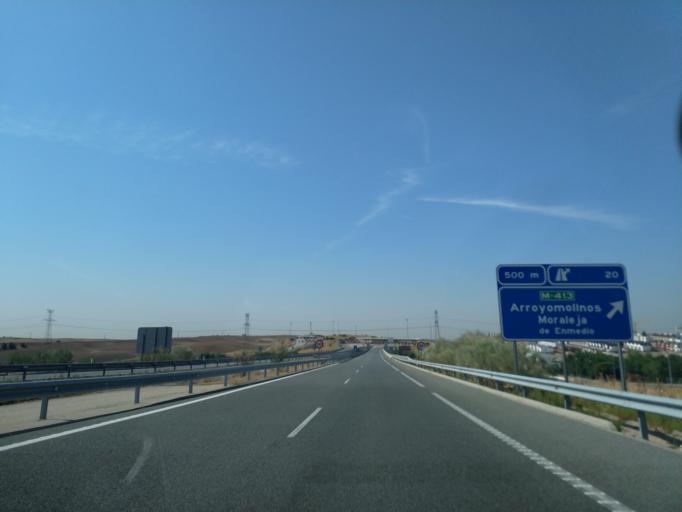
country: ES
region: Madrid
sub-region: Provincia de Madrid
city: Arroyomolinos
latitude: 40.2630
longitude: -3.9031
